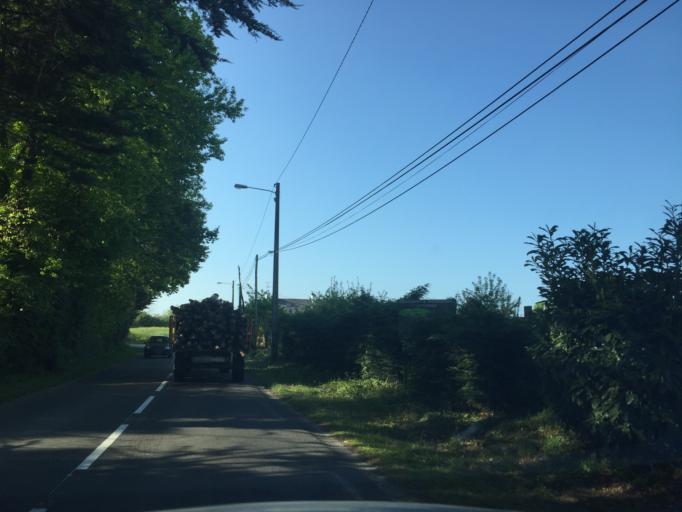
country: FR
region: Brittany
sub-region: Departement des Cotes-d'Armor
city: Saint-Cast-le-Guildo
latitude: 48.5988
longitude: -2.2505
